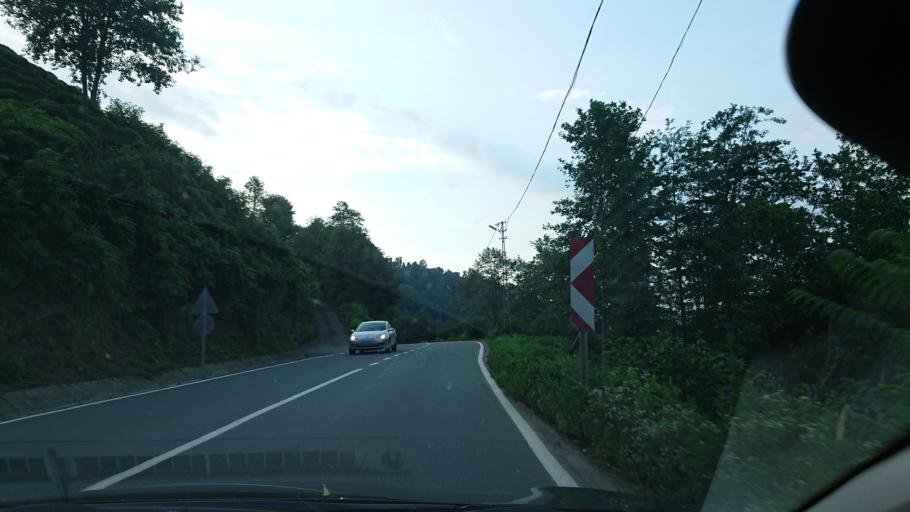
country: TR
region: Rize
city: Cayeli
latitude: 41.0675
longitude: 40.7137
